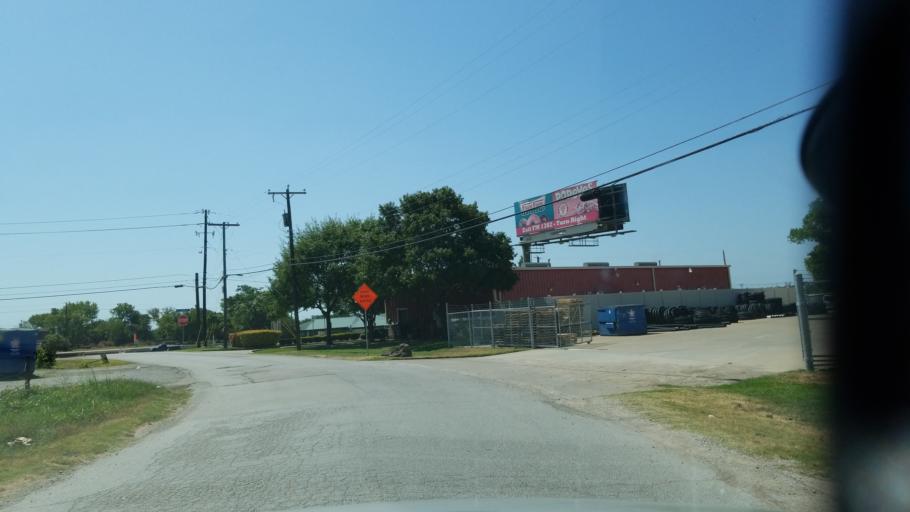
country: US
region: Texas
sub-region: Dallas County
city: Duncanville
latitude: 32.6358
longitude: -96.8990
